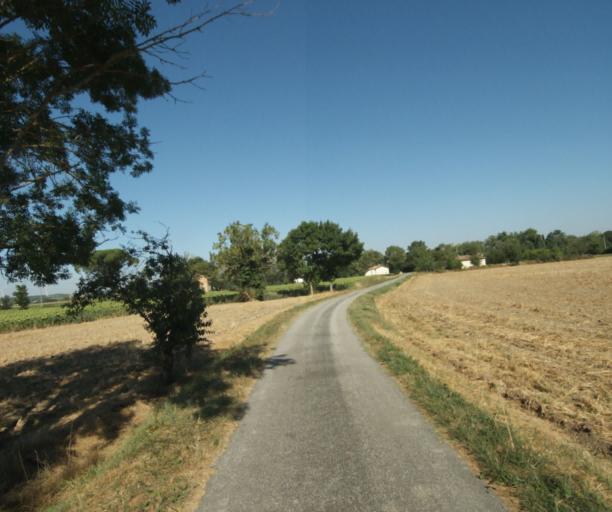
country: FR
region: Midi-Pyrenees
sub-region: Departement de la Haute-Garonne
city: Revel
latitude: 43.4683
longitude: 1.9576
